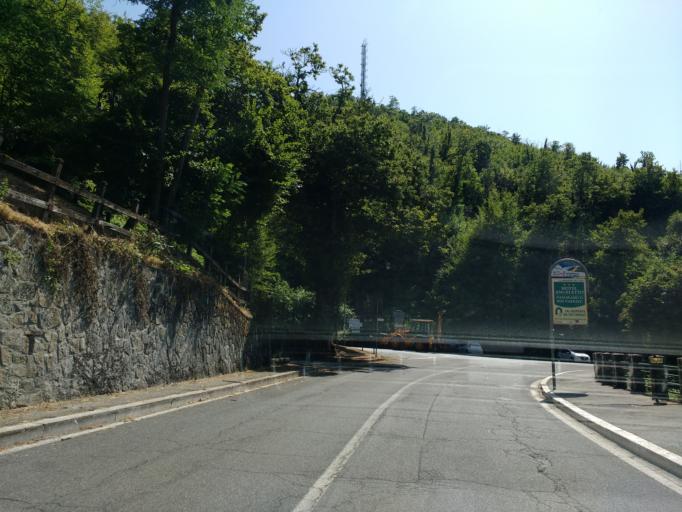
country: IT
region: Latium
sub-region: Citta metropolitana di Roma Capitale
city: Rocca di Papa
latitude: 41.7546
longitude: 12.7055
